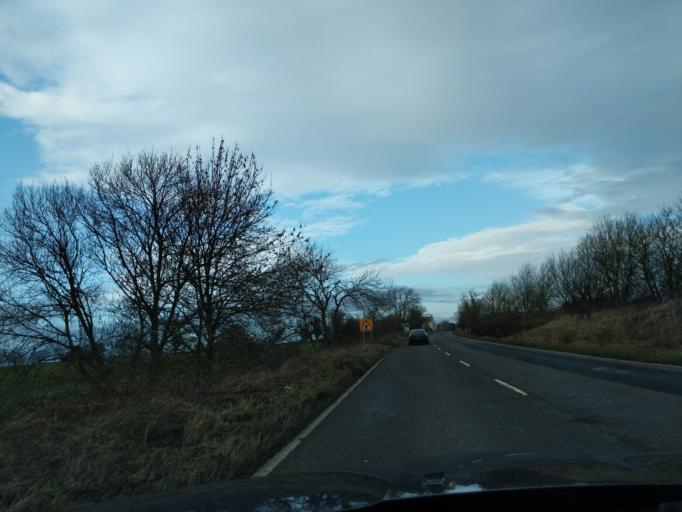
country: GB
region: England
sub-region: Northumberland
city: Meldon
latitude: 55.0819
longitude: -1.8073
